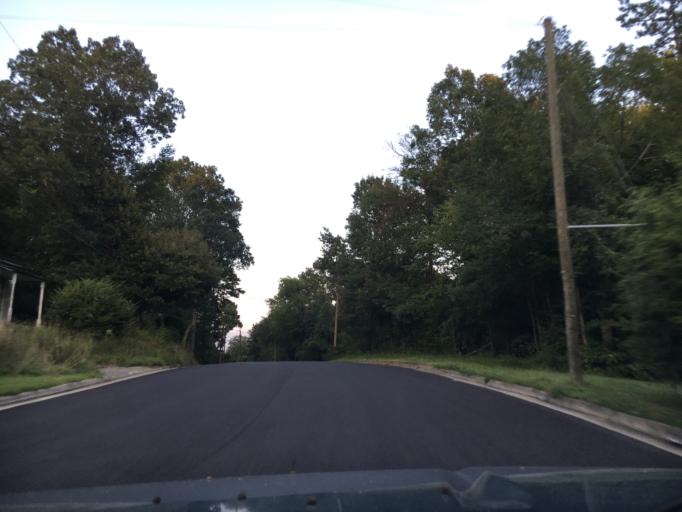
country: US
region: Virginia
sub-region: Halifax County
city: South Boston
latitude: 36.7091
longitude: -78.9038
